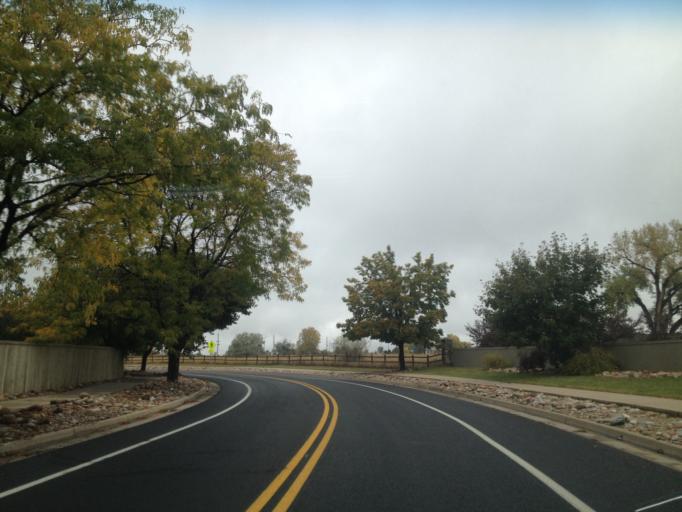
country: US
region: Colorado
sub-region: Boulder County
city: Superior
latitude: 39.9778
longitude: -105.1631
